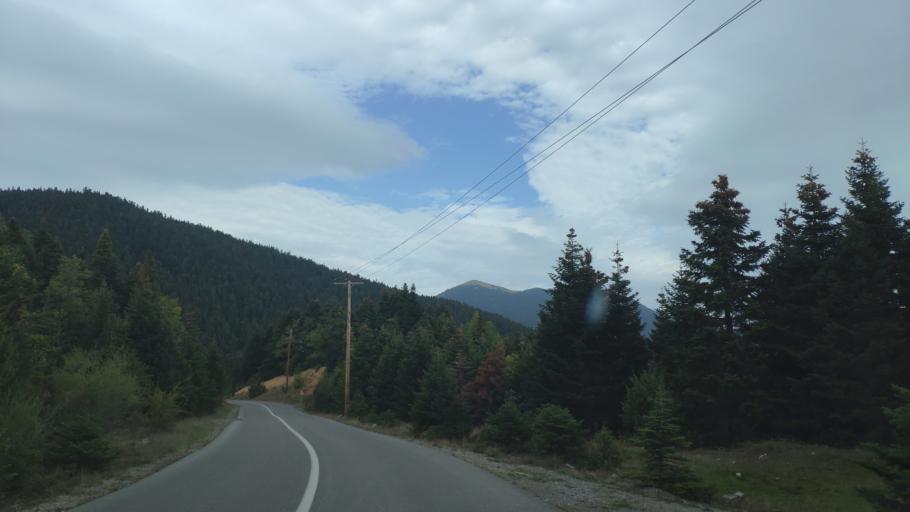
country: GR
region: Central Greece
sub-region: Nomos Fokidos
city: Amfissa
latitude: 38.7073
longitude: 22.3269
